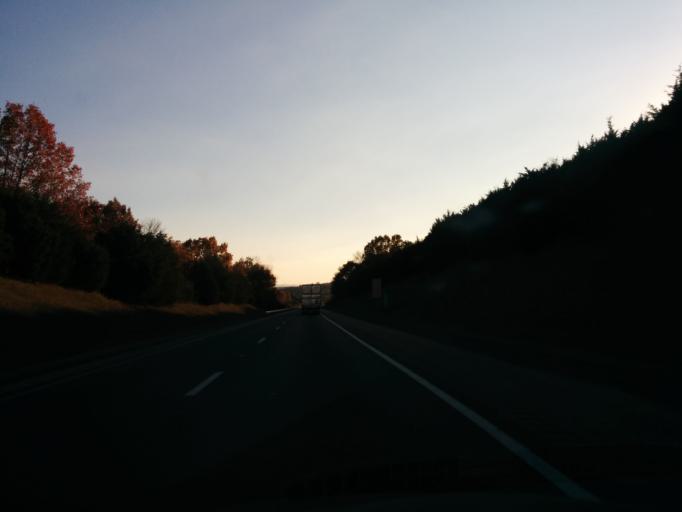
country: US
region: Virginia
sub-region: Rockbridge County
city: East Lexington
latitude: 37.8024
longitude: -79.3924
